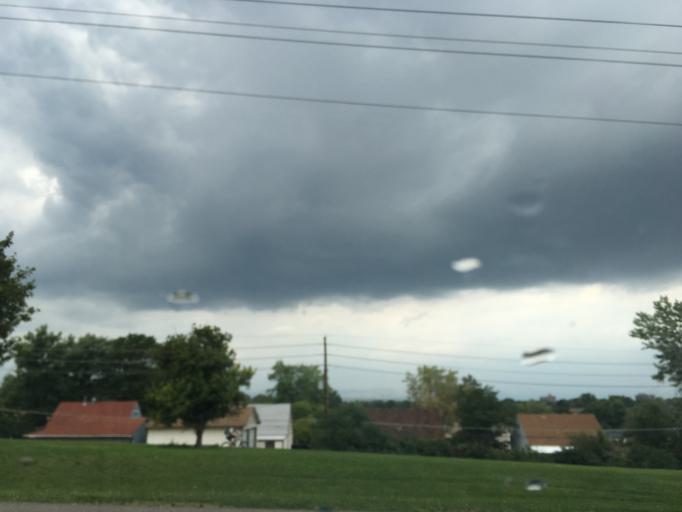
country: US
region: Colorado
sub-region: Arapahoe County
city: Englewood
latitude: 39.6877
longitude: -105.0058
